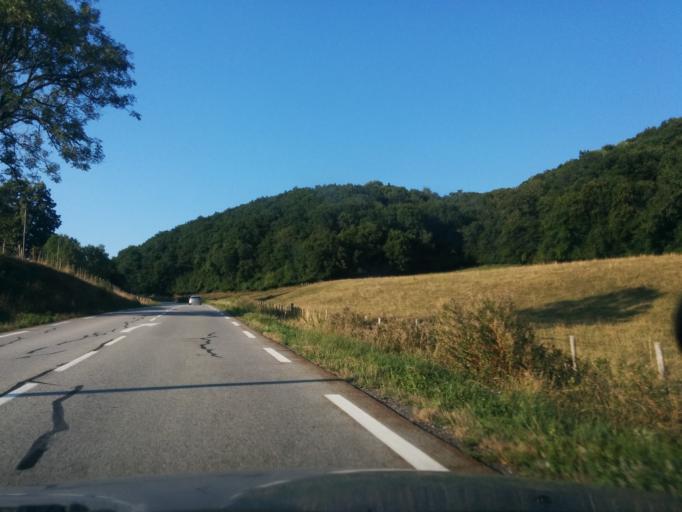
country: FR
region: Rhone-Alpes
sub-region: Departement de l'Isere
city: Bilieu
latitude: 45.4484
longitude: 5.5665
